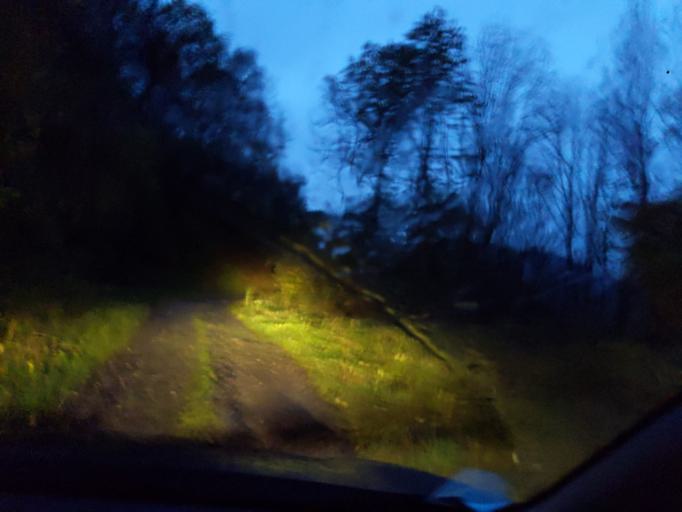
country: FR
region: Rhone-Alpes
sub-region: Departement de la Savoie
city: Aiton
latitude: 45.5165
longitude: 6.3402
